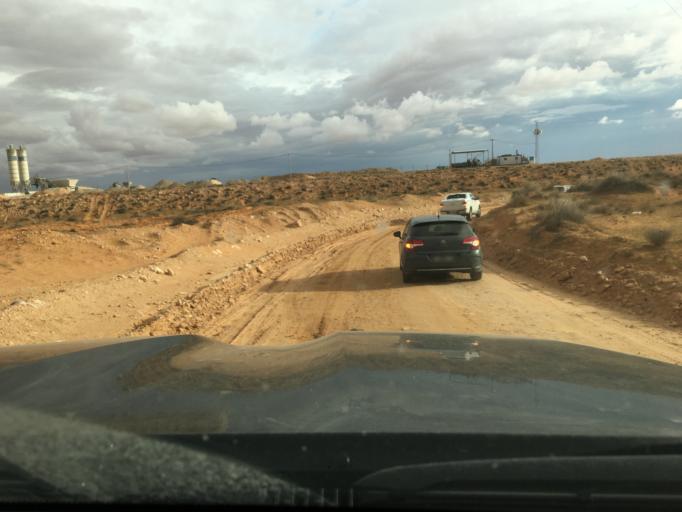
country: TN
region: Madanin
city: Medenine
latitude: 33.2687
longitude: 10.5691
